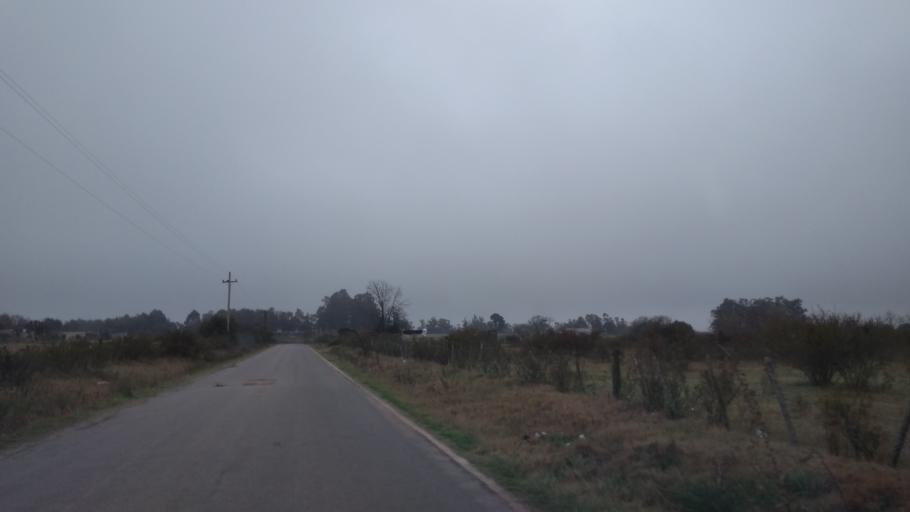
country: UY
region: Florida
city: Florida
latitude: -34.0839
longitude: -56.2055
